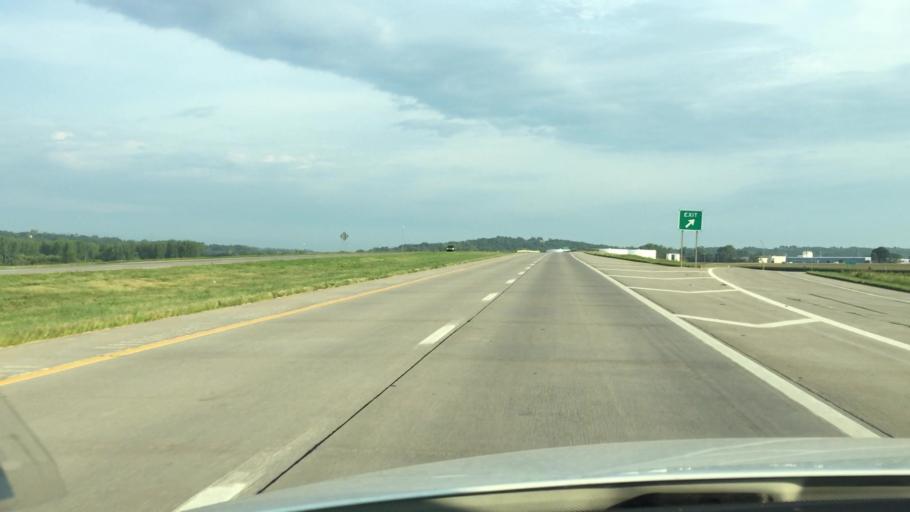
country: US
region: Kansas
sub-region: Doniphan County
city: Wathena
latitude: 39.7448
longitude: -94.9222
